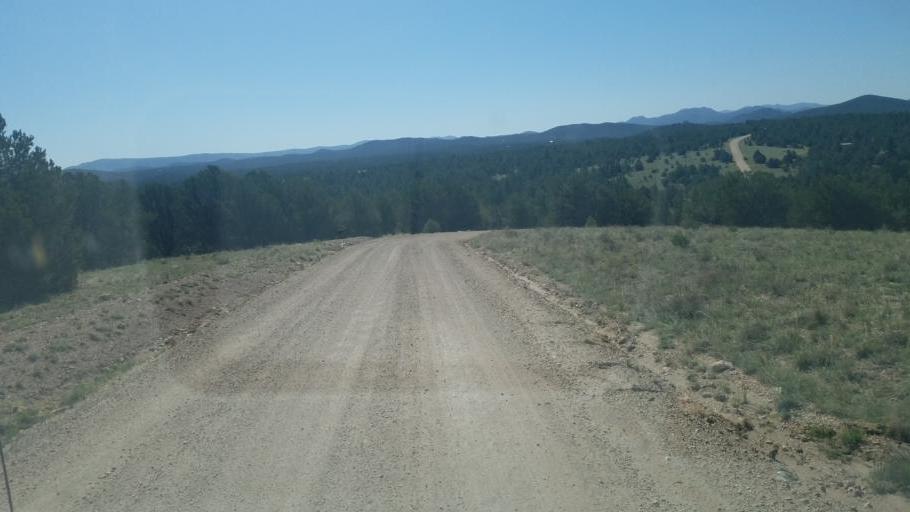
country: US
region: Colorado
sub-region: Custer County
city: Westcliffe
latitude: 38.2887
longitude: -105.4530
